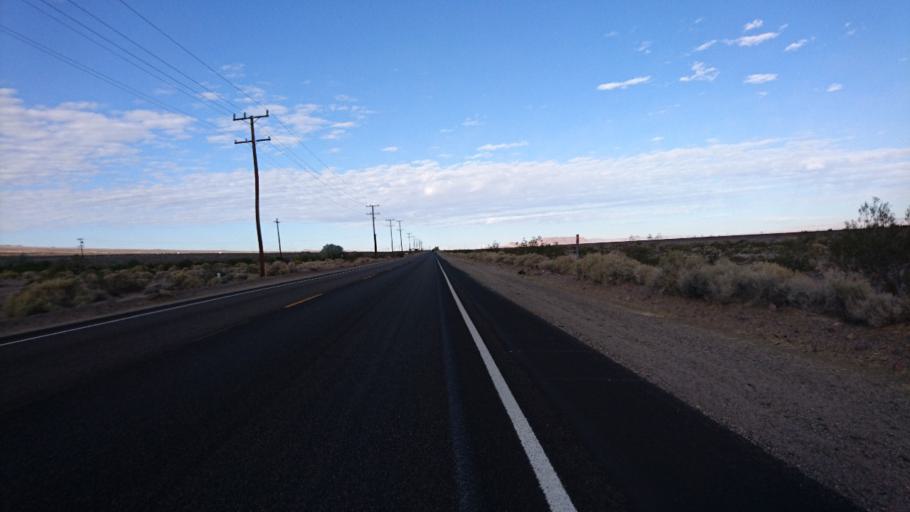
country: US
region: California
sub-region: San Bernardino County
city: Barstow
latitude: 34.8465
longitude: -116.7830
